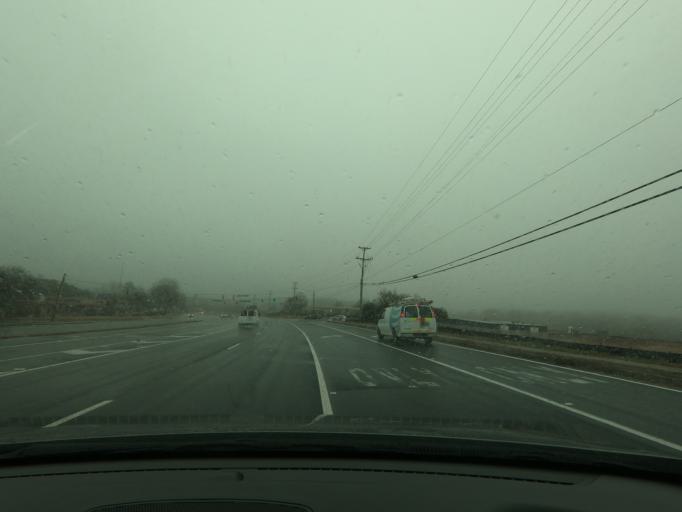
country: US
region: Georgia
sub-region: Fulton County
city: Alpharetta
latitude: 34.1118
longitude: -84.2218
